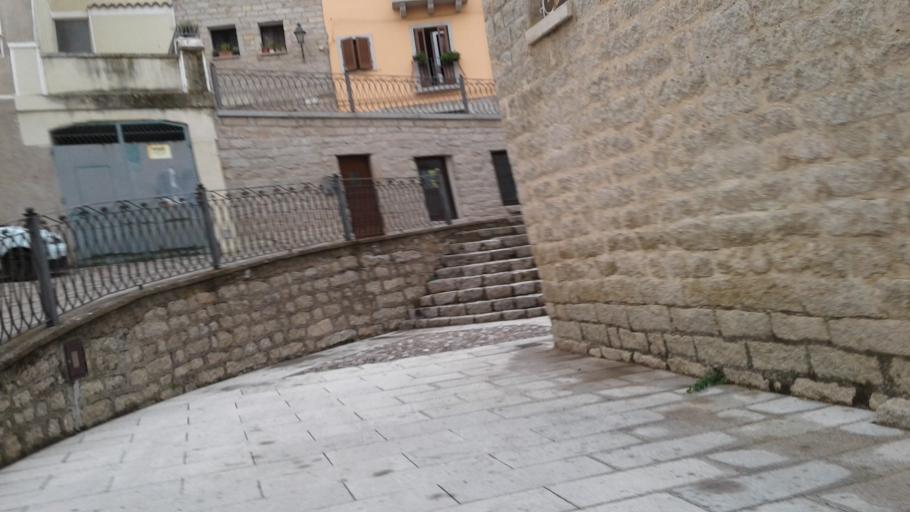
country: IT
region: Sardinia
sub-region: Provincia di Olbia-Tempio
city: Aggius
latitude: 40.9298
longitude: 9.0652
